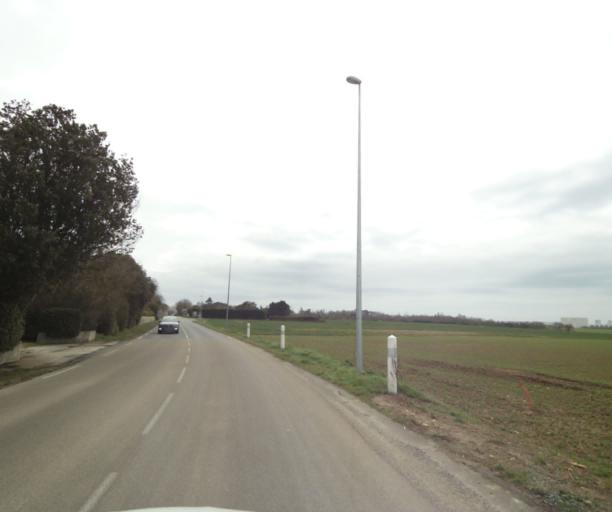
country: FR
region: Poitou-Charentes
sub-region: Departement de la Charente-Maritime
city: Nieul-sur-Mer
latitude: 46.1866
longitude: -1.1800
